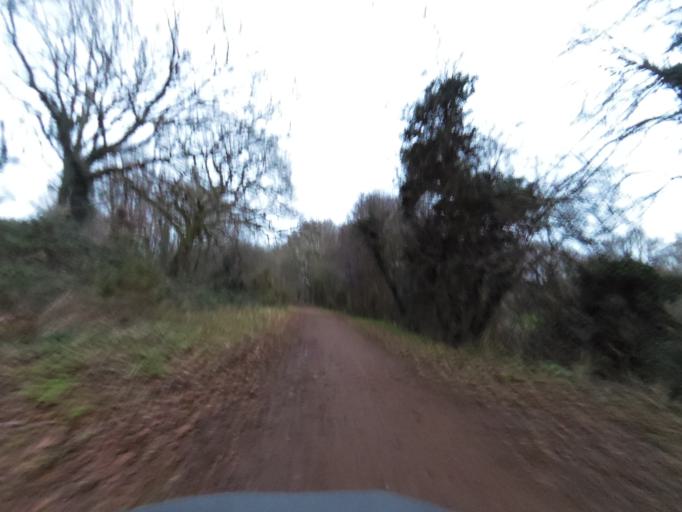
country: GB
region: England
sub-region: Norfolk
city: Costessey
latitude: 52.6891
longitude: 1.2073
